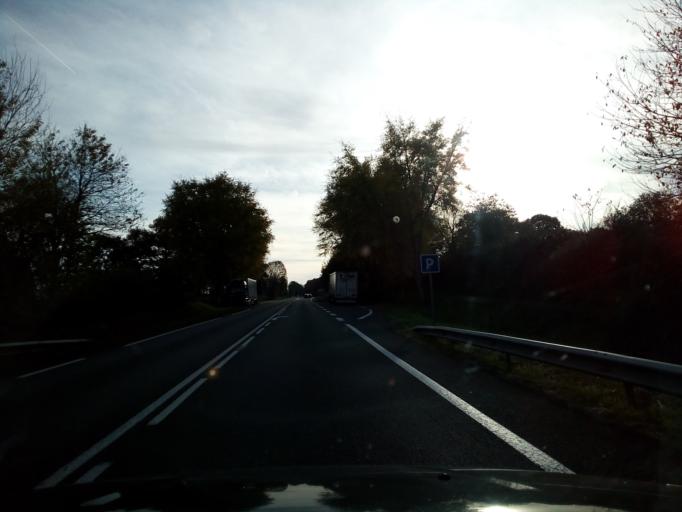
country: FR
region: Poitou-Charentes
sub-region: Departement de la Charente
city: Confolens
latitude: 45.9988
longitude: 0.6326
